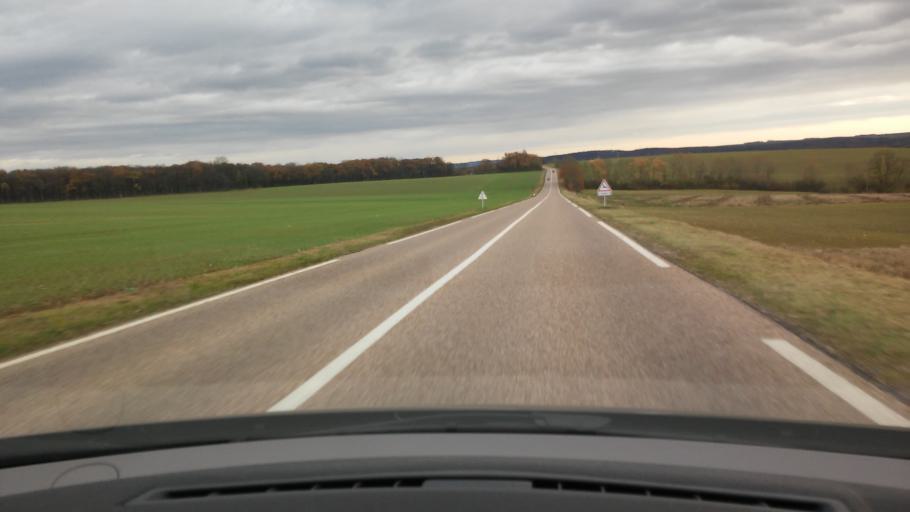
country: FR
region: Lorraine
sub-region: Departement de la Moselle
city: Retonfey
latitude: 49.1493
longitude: 6.3388
